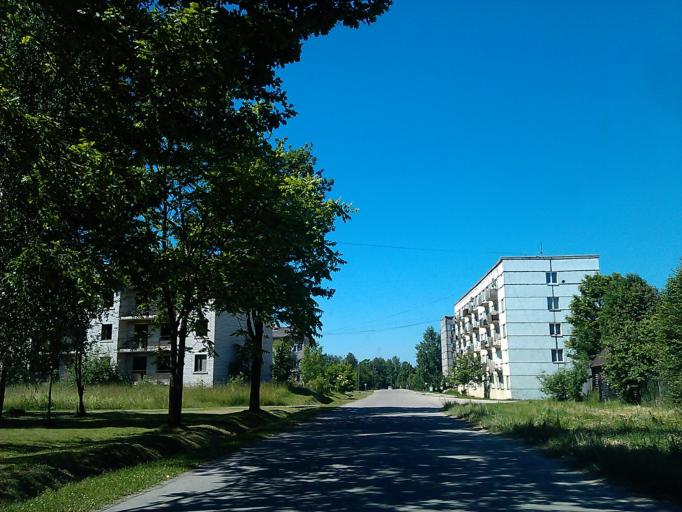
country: LV
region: Vilanu
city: Vilani
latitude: 56.5451
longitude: 26.9328
